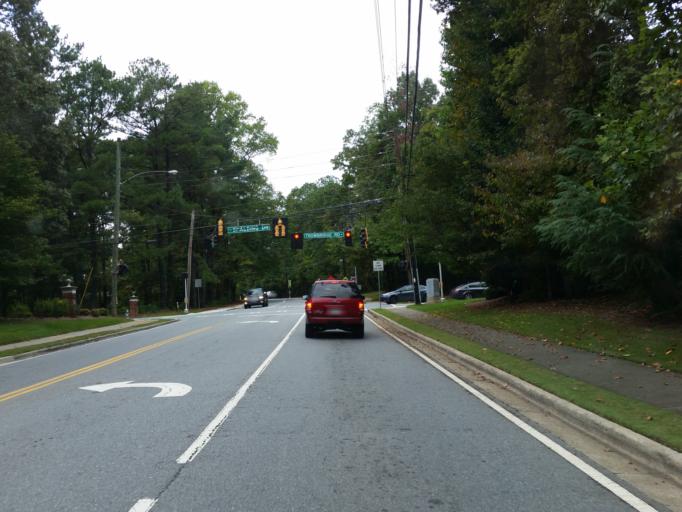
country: US
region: Georgia
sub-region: DeKalb County
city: Dunwoody
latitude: 33.9563
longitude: -84.3583
